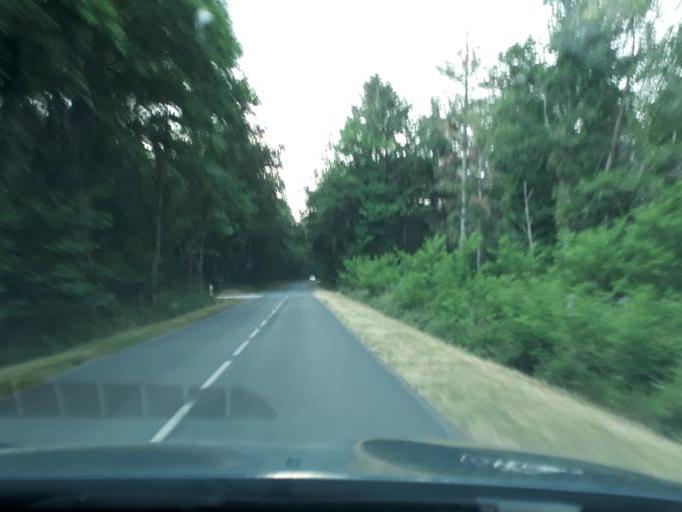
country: FR
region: Centre
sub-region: Departement du Loiret
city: Marcilly-en-Villette
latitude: 47.7535
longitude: 2.0552
